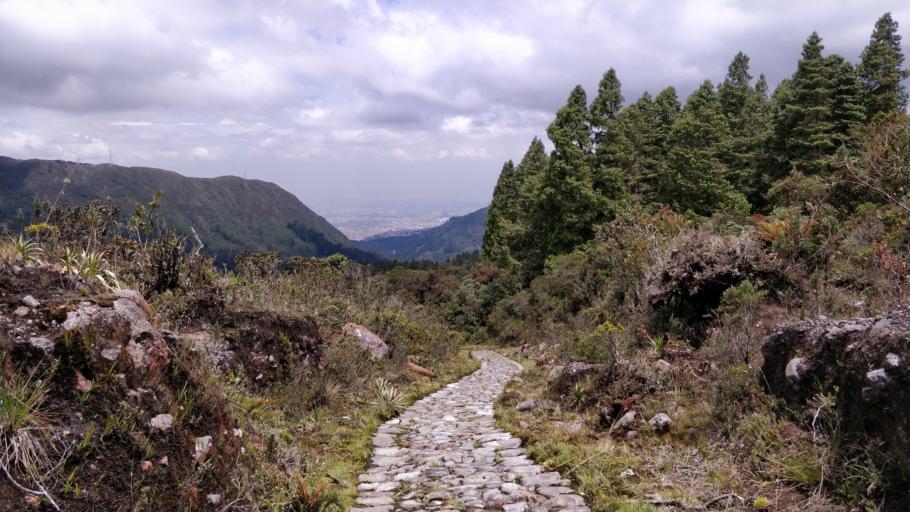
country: CO
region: Bogota D.C.
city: Bogota
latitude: 4.5320
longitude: -74.0487
